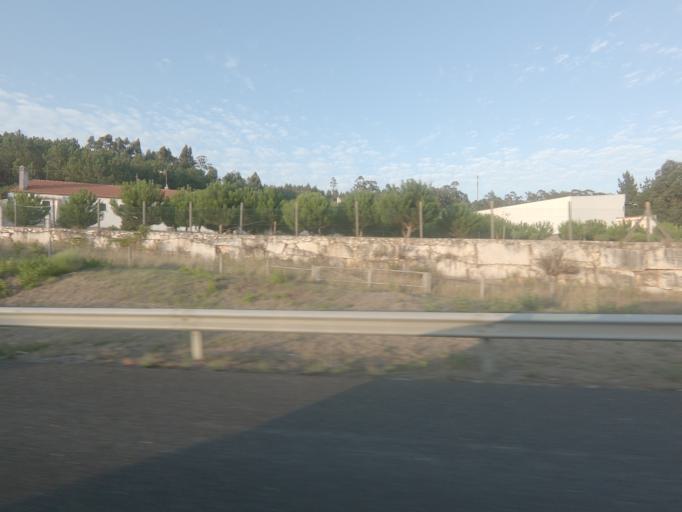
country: PT
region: Leiria
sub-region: Leiria
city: Santa Catarina da Serra
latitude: 39.7087
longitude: -8.7080
